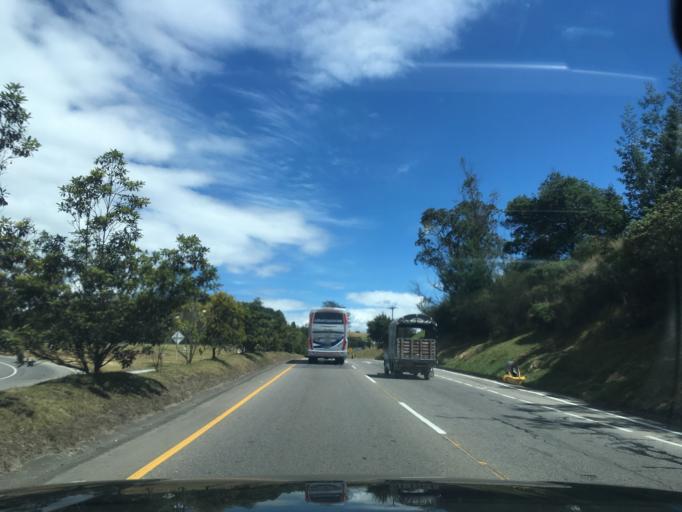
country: CO
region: Cundinamarca
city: Choconta
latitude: 5.0904
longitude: -73.7200
